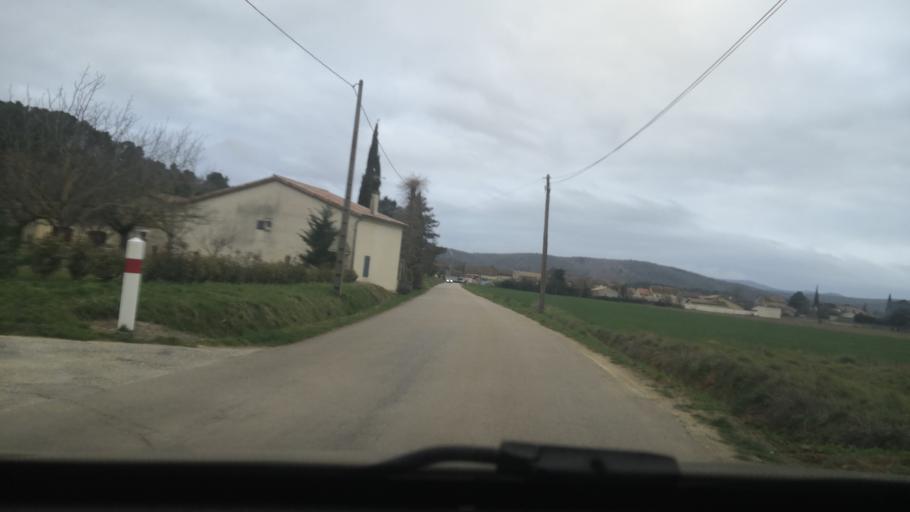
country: FR
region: Rhone-Alpes
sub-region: Departement de la Drome
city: Montboucher-sur-Jabron
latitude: 44.5575
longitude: 4.8643
